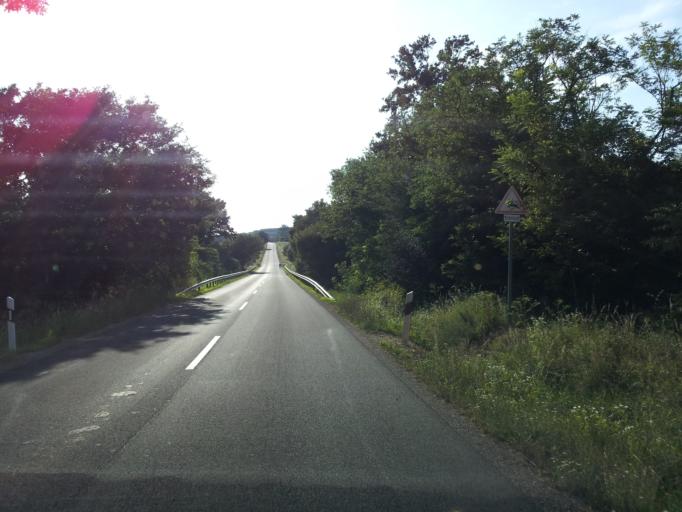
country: HU
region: Veszprem
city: Urkut
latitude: 47.0017
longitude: 17.6438
